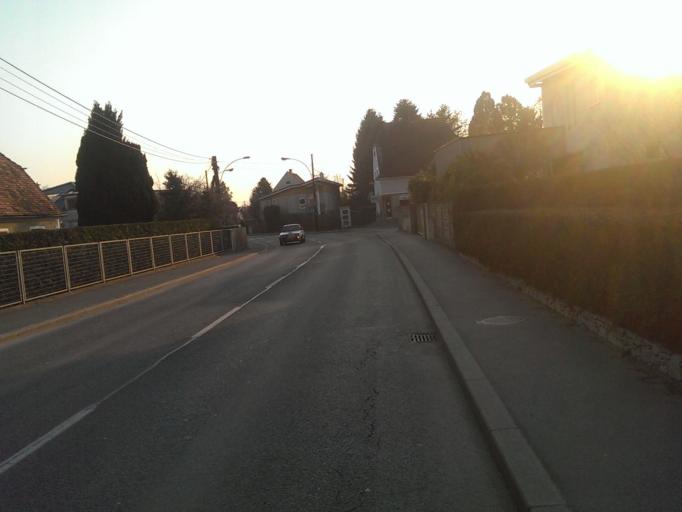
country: AT
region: Styria
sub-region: Graz Stadt
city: Graz
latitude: 47.0530
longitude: 15.4711
